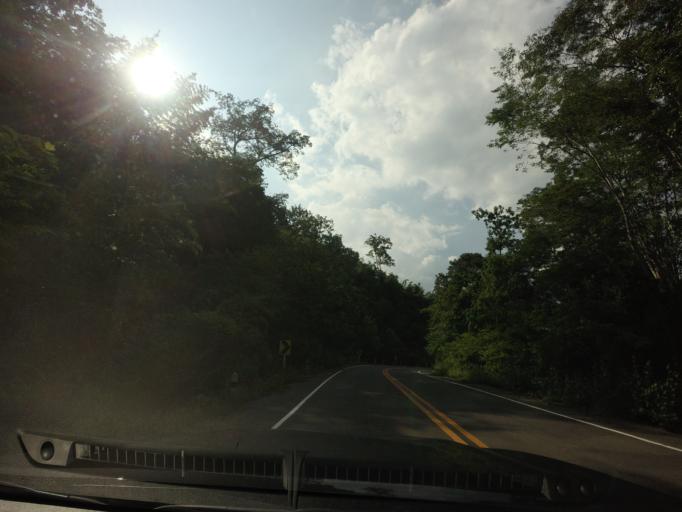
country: TH
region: Nan
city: Na Noi
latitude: 18.2761
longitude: 100.9601
